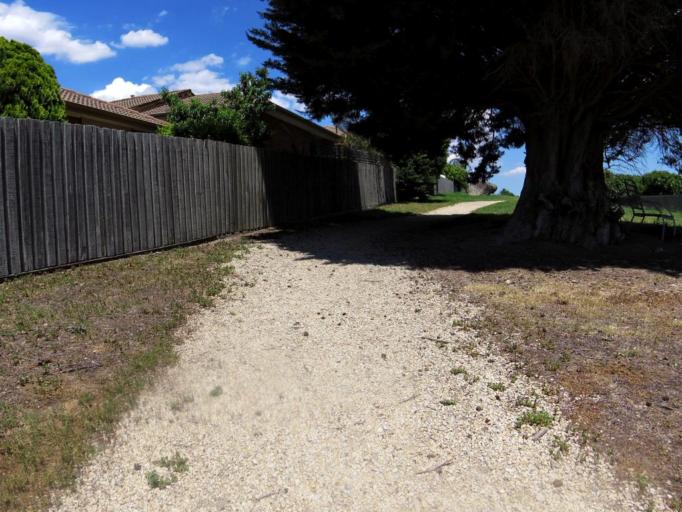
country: AU
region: Victoria
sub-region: Casey
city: Endeavour Hills
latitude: -37.9750
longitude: 145.2532
